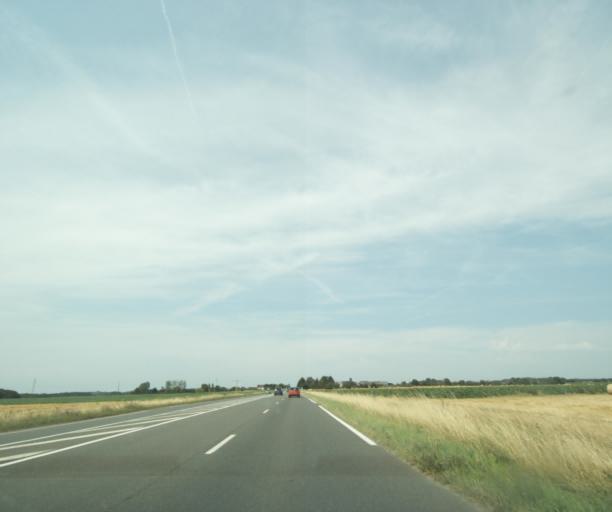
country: FR
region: Centre
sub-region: Departement d'Indre-et-Loire
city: Sorigny
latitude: 47.2017
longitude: 0.6715
